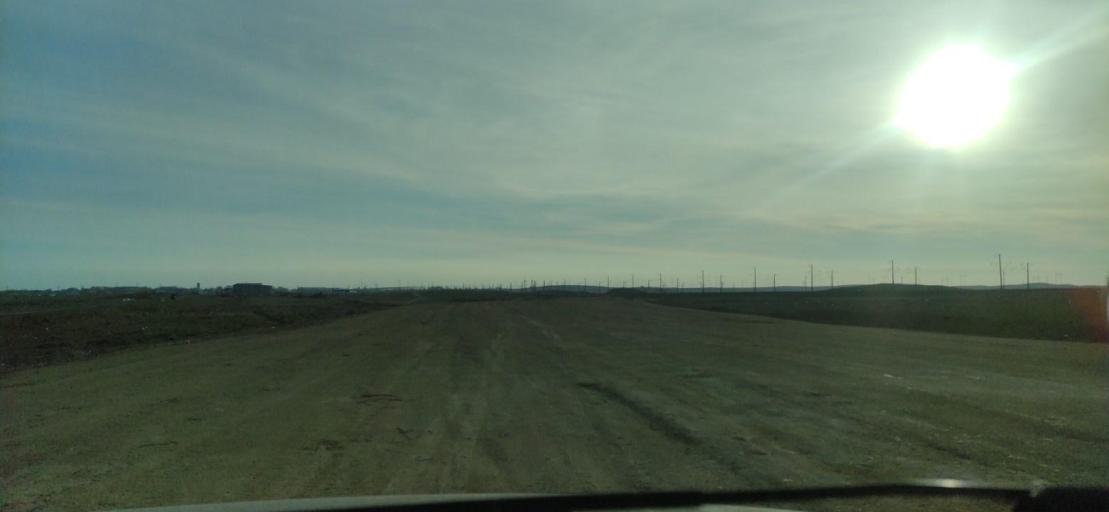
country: KZ
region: Qaraghandy
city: Saryshaghan
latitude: 46.1439
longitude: 73.6085
